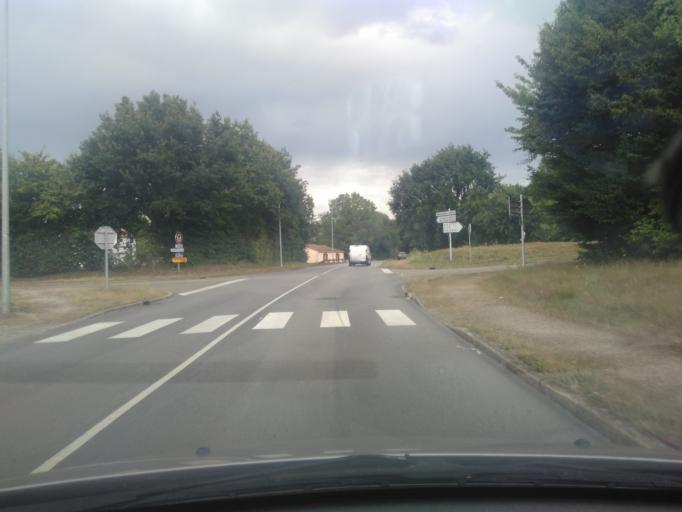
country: FR
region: Pays de la Loire
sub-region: Departement de la Vendee
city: La Roche-sur-Yon
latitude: 46.6908
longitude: -1.4396
